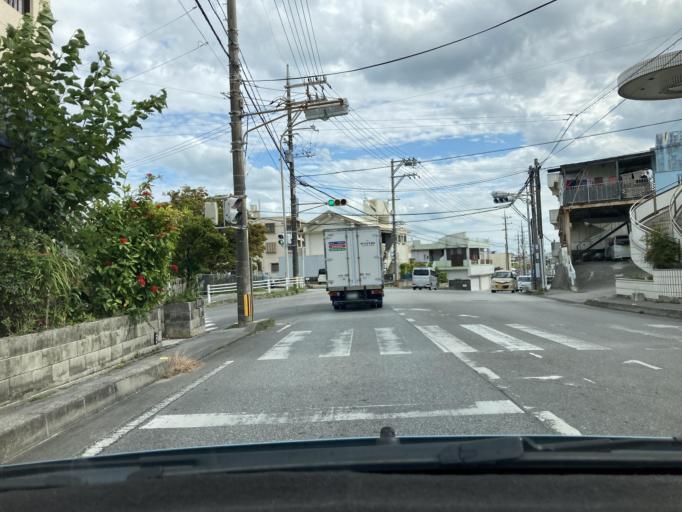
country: JP
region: Okinawa
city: Gushikawa
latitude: 26.3535
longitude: 127.8347
